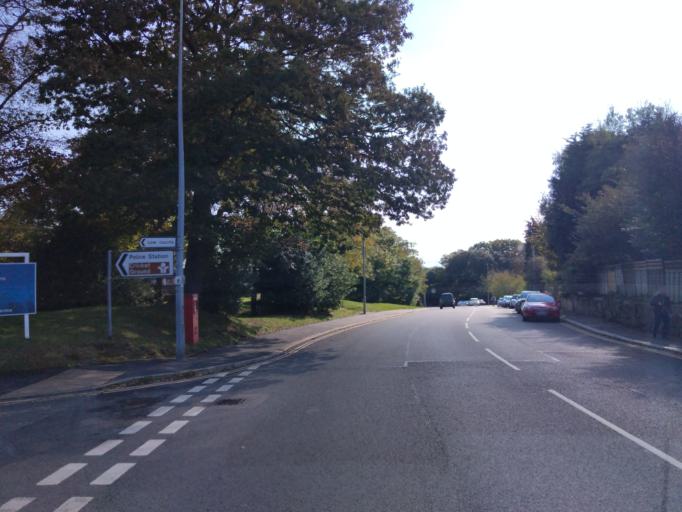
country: GB
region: England
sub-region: East Sussex
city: Hastings
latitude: 50.8590
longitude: 0.5647
